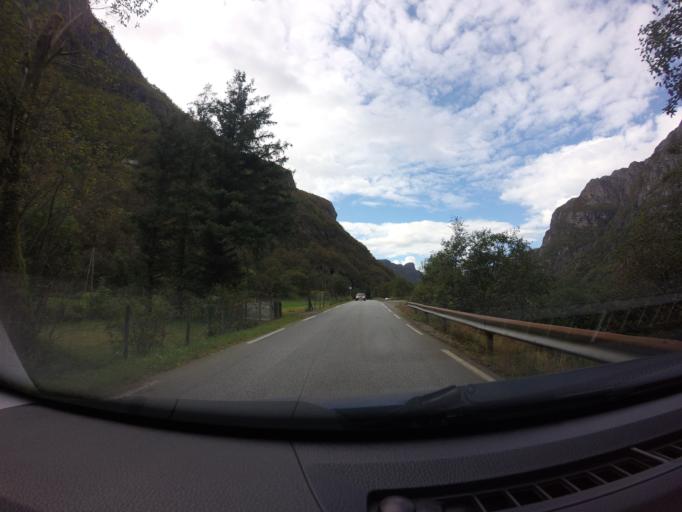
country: NO
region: Rogaland
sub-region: Forsand
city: Forsand
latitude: 58.8416
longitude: 6.3188
